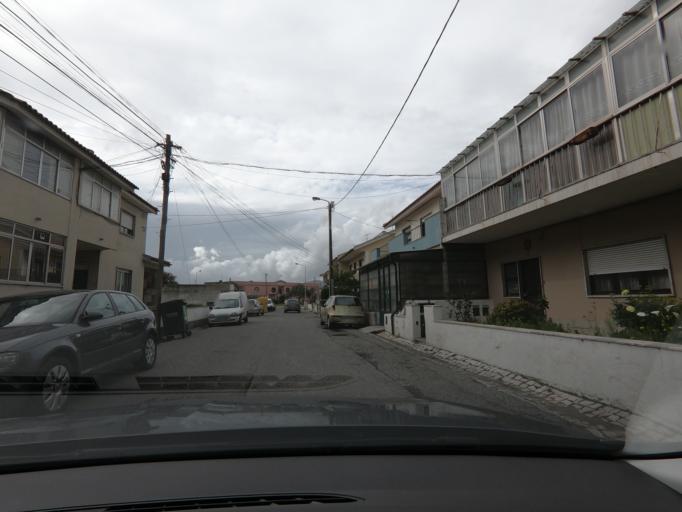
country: PT
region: Lisbon
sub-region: Sintra
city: Rio de Mouro
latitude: 38.7379
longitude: -9.3389
